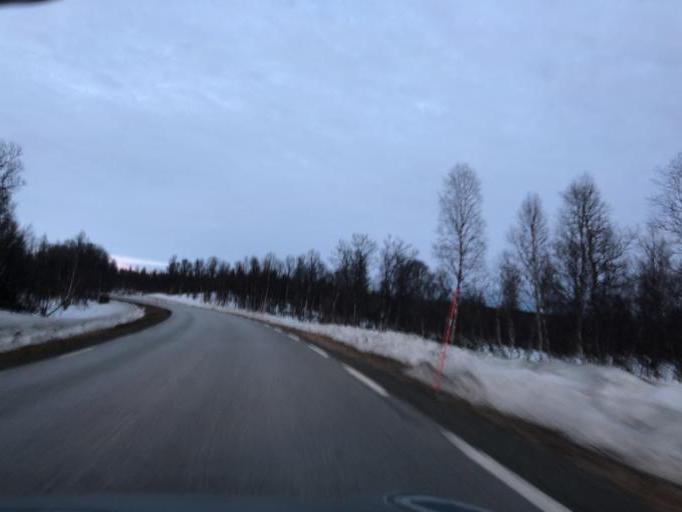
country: NO
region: Sor-Trondelag
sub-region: Tydal
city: Aas
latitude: 62.6995
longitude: 11.7954
